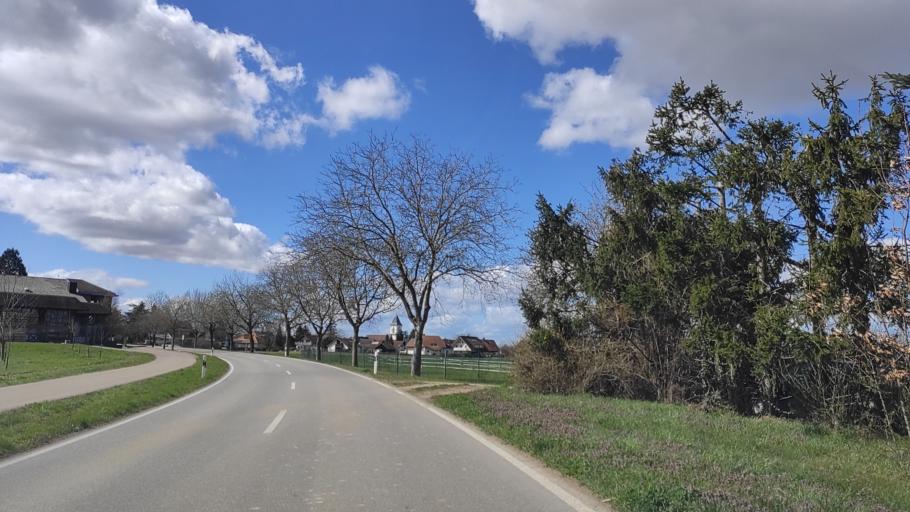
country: DE
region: Baden-Wuerttemberg
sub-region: Freiburg Region
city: Heitersheim
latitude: 47.8728
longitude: 7.6745
